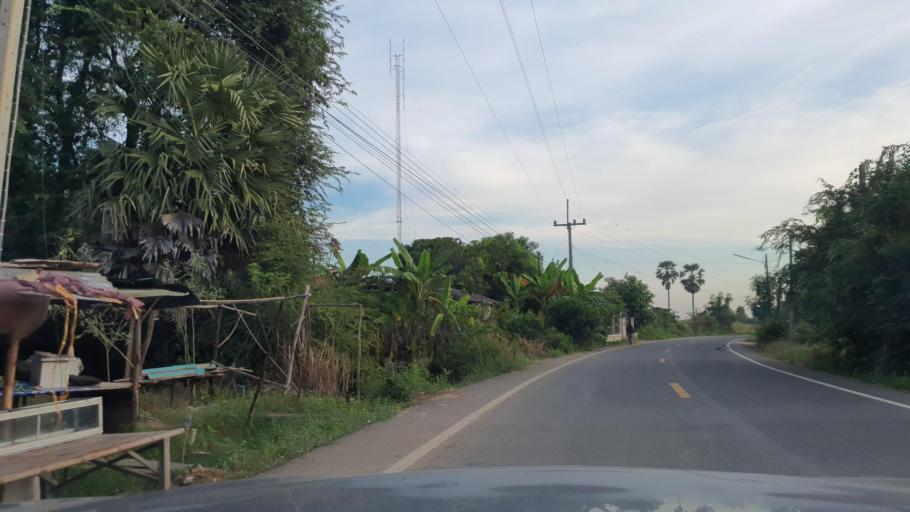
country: TH
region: Uthai Thani
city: Sawang Arom
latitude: 15.7116
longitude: 99.9496
